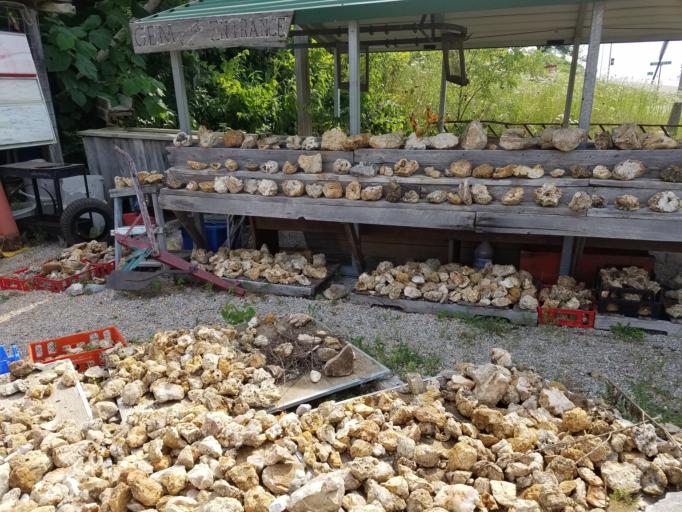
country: US
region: Kentucky
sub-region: Barren County
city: Cave City
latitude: 37.1361
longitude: -85.9834
